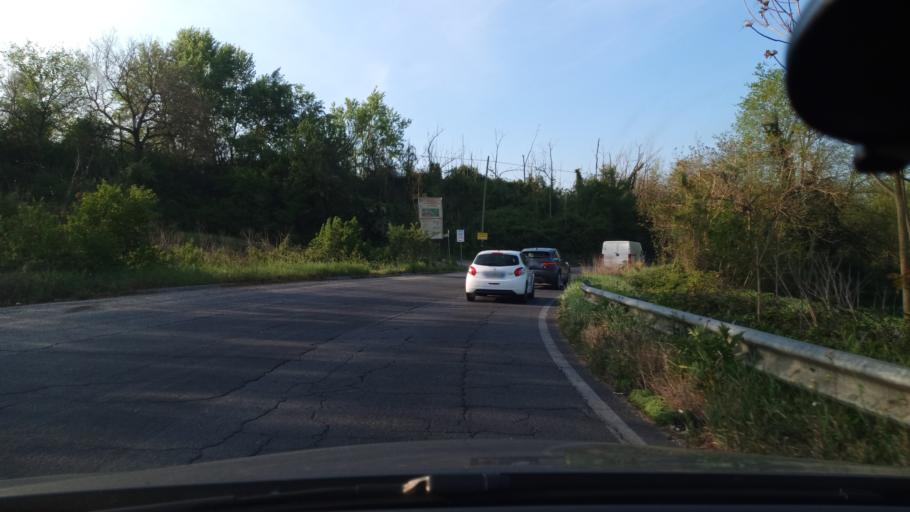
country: IT
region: Latium
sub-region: Citta metropolitana di Roma Capitale
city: Fiano Romano
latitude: 42.1778
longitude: 12.6375
